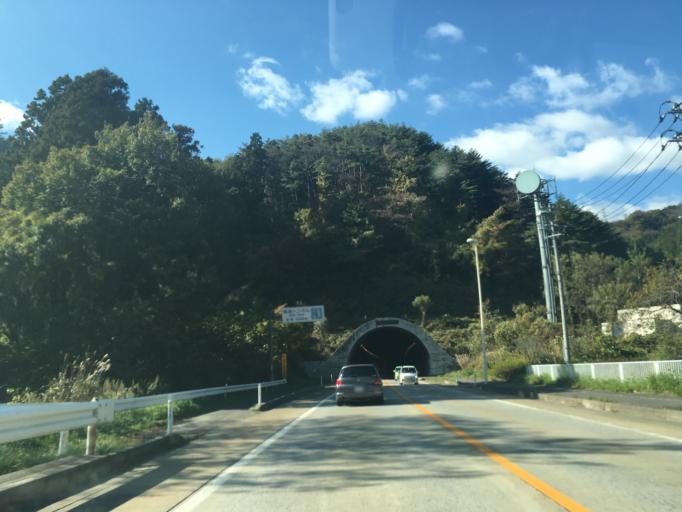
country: JP
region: Fukushima
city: Motomiya
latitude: 37.4891
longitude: 140.2744
